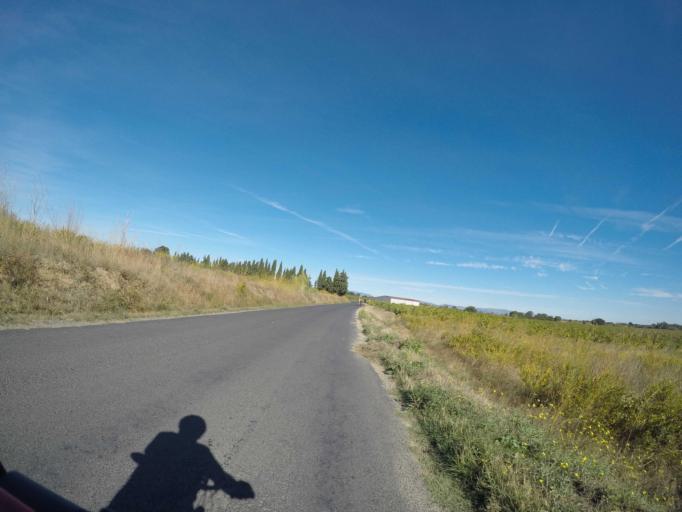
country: FR
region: Languedoc-Roussillon
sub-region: Departement des Pyrenees-Orientales
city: Ponteilla
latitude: 42.6315
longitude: 2.8102
